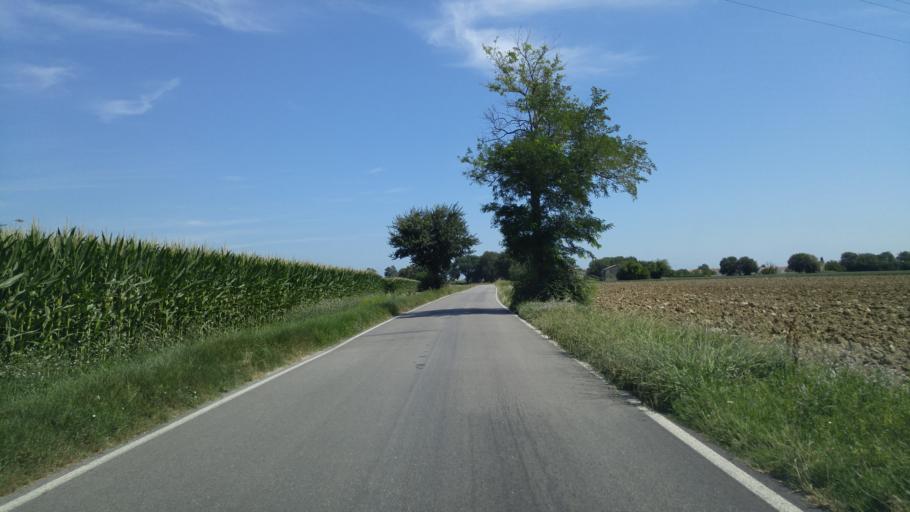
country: IT
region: The Marches
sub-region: Provincia di Pesaro e Urbino
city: Cuccurano
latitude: 43.7936
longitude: 12.9808
